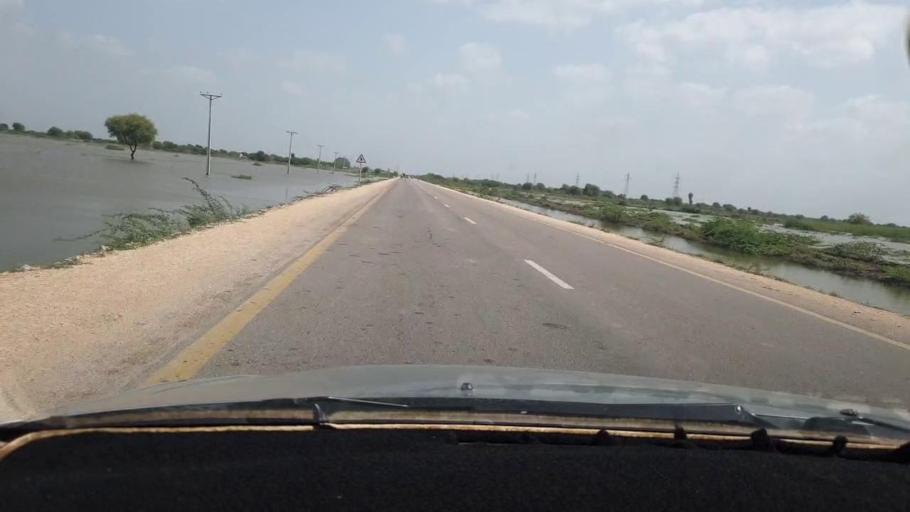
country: PK
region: Sindh
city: Digri
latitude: 25.0462
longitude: 69.2285
